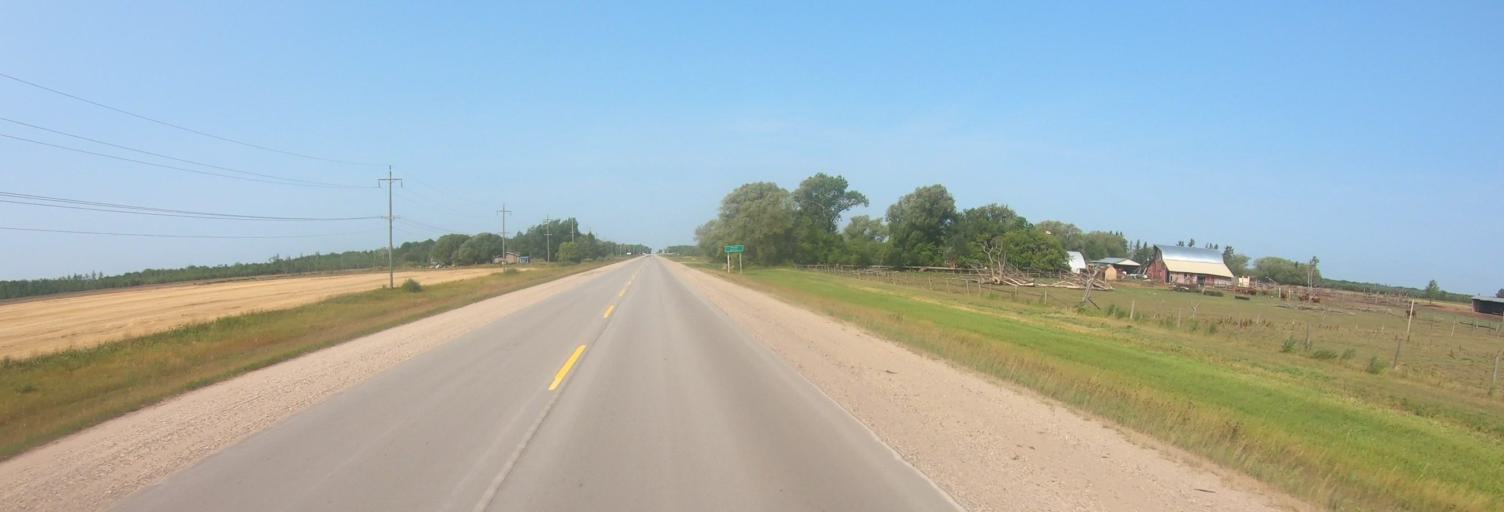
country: US
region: Minnesota
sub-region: Roseau County
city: Roseau
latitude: 49.0896
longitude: -95.9623
